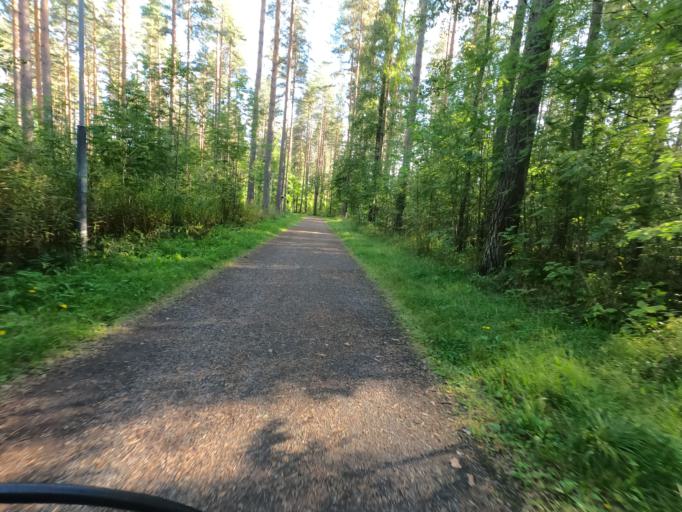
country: FI
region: North Karelia
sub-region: Joensuu
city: Joensuu
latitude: 62.6152
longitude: 29.7525
